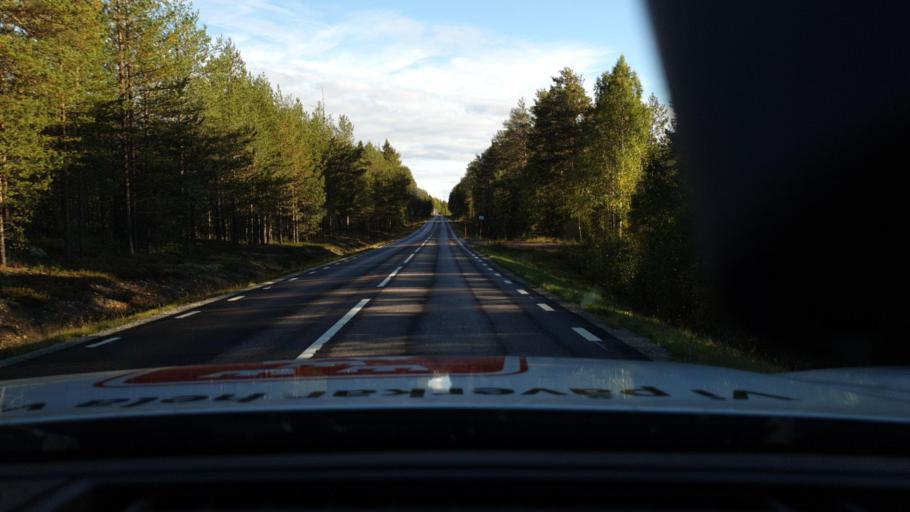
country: SE
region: Norrbotten
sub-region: Overkalix Kommun
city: OEverkalix
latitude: 66.4409
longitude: 22.7884
